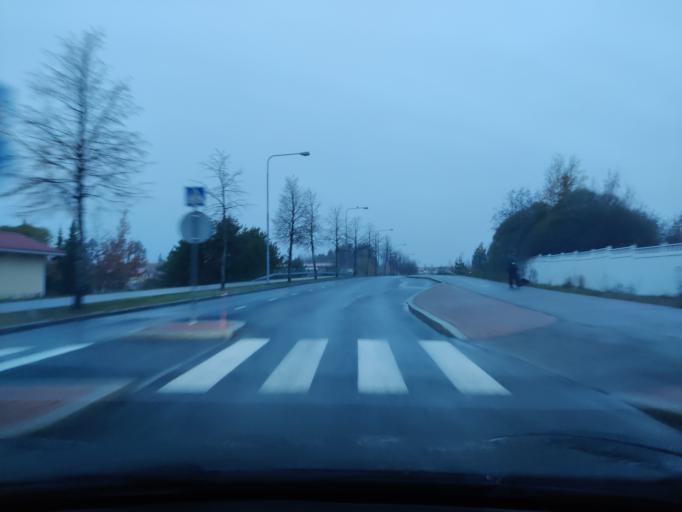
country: FI
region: Northern Savo
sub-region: Kuopio
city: Kuopio
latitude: 62.8257
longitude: 27.6922
